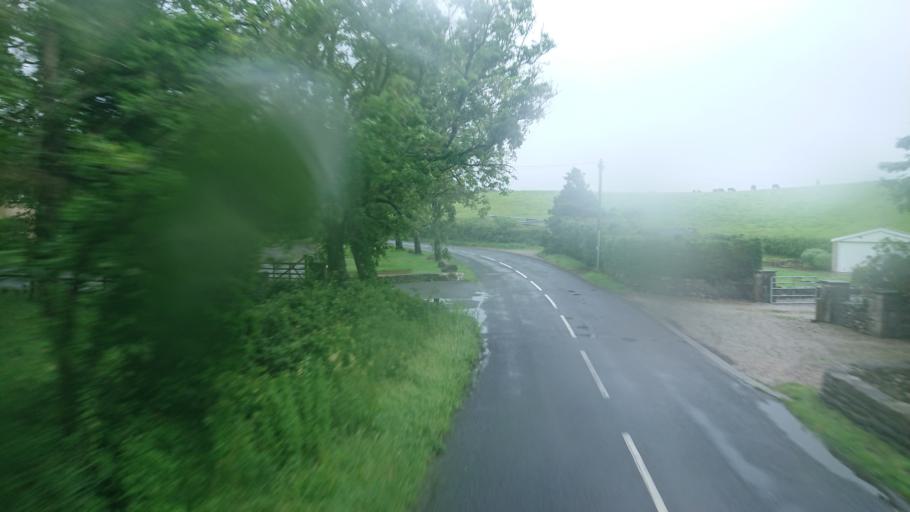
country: GB
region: England
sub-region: Cumbria
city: Milnthorpe
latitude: 54.2146
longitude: -2.7491
